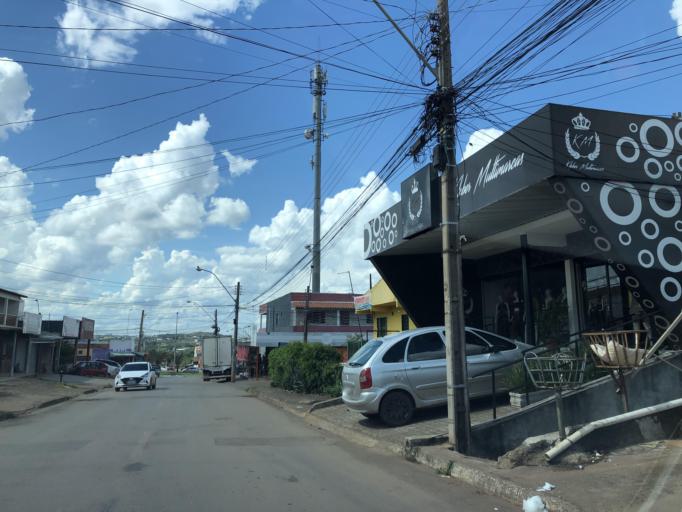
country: BR
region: Federal District
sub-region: Brasilia
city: Brasilia
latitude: -15.8996
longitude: -47.7827
